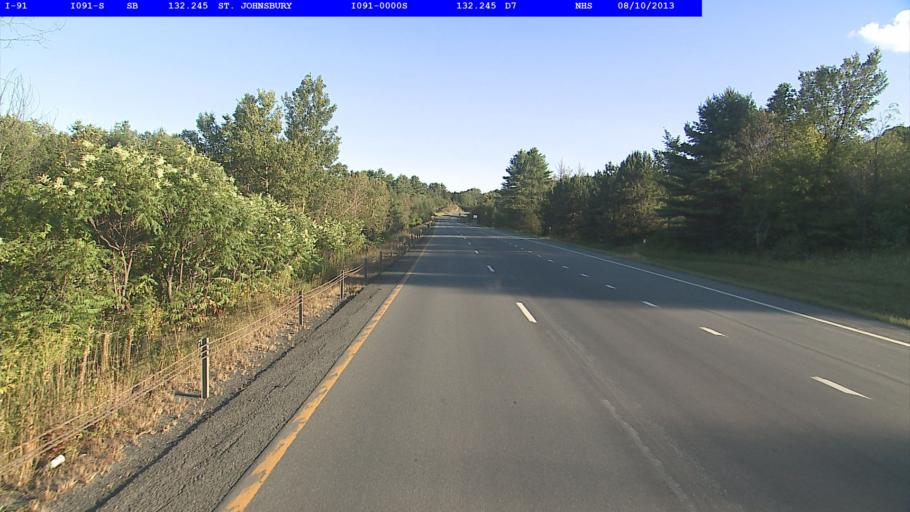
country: US
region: Vermont
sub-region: Caledonia County
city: St Johnsbury
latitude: 44.4491
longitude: -72.0250
